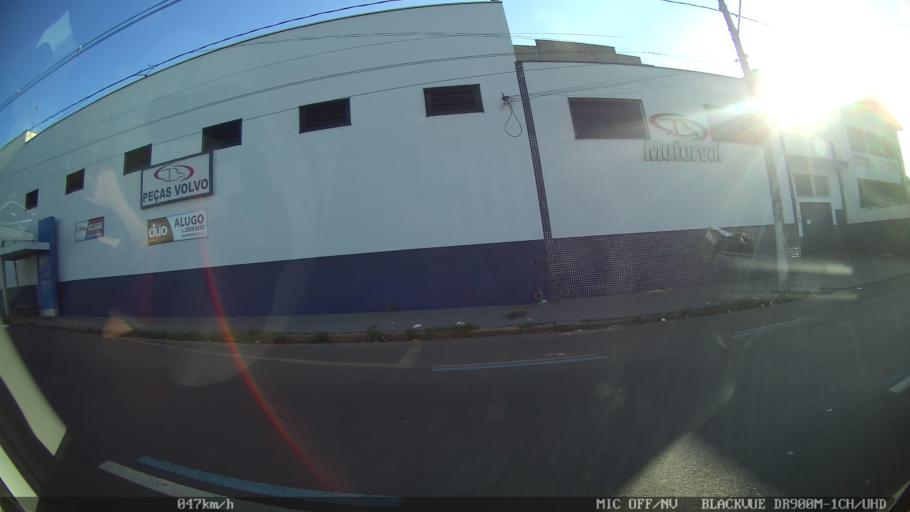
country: BR
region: Sao Paulo
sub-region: Piracicaba
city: Piracicaba
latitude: -22.7508
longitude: -47.6441
